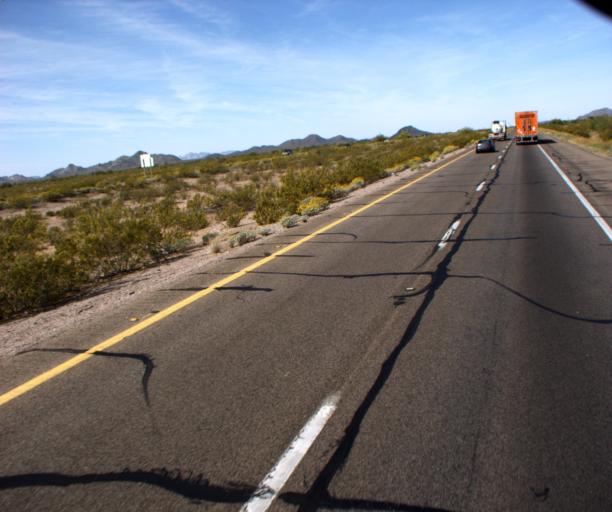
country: US
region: Arizona
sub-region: Maricopa County
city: Buckeye
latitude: 33.5019
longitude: -112.9580
